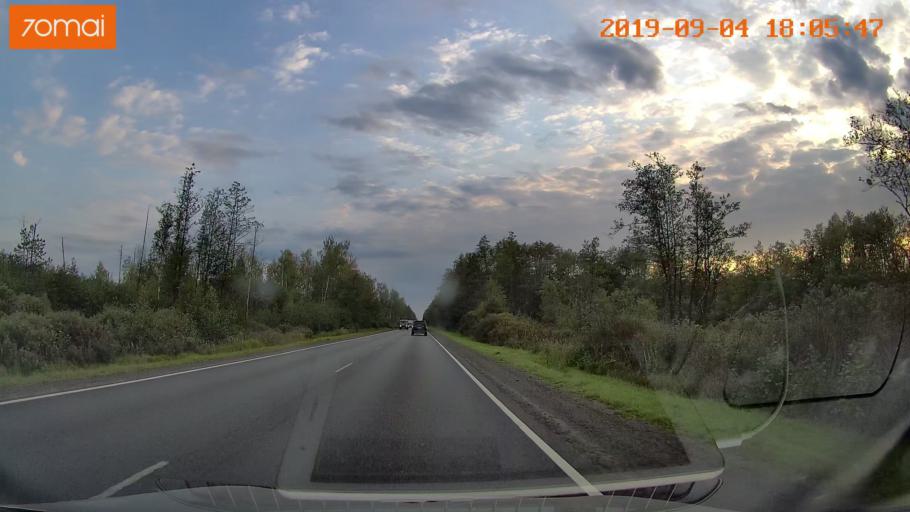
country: RU
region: Moskovskaya
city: Il'inskiy Pogost
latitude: 55.4377
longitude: 38.8223
